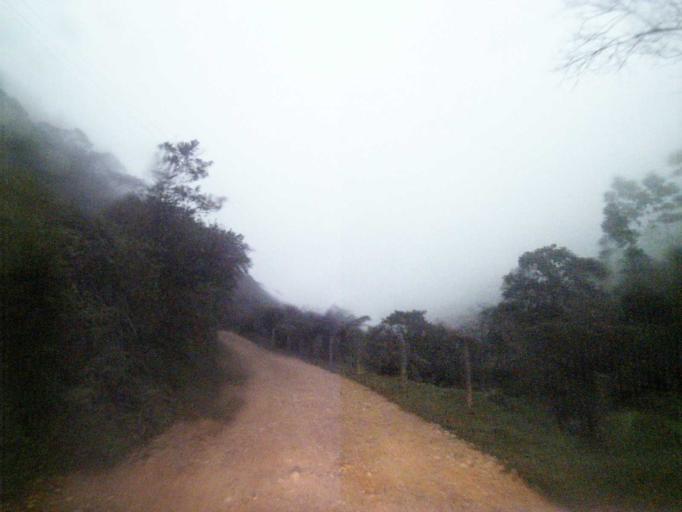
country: BR
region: Santa Catarina
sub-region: Anitapolis
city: Anitapolis
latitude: -27.7903
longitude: -49.1379
